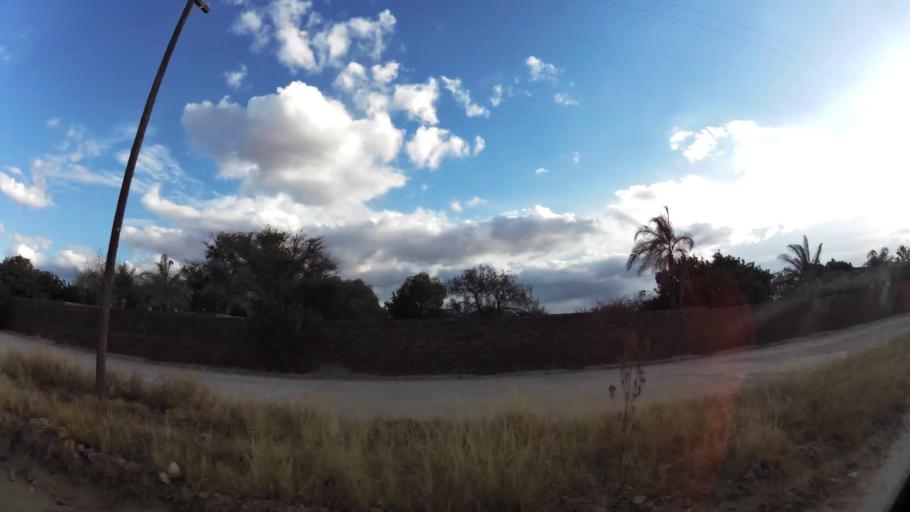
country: ZA
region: Limpopo
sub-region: Capricorn District Municipality
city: Polokwane
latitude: -23.9250
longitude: 29.4357
